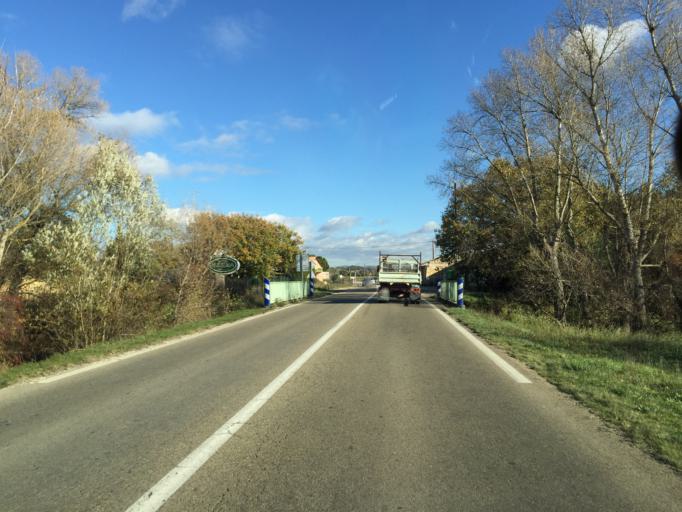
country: FR
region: Provence-Alpes-Cote d'Azur
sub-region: Departement du Vaucluse
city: Roussillon
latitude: 43.8629
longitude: 5.2902
